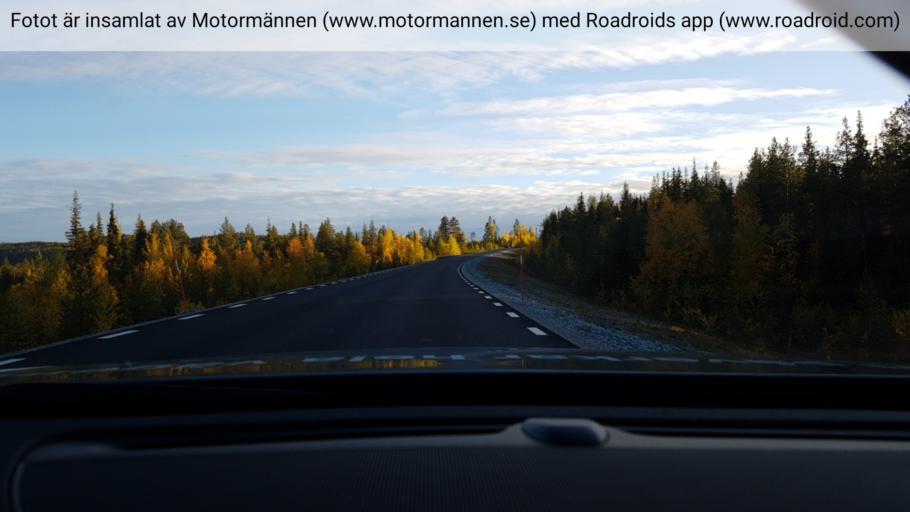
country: SE
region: Norrbotten
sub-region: Jokkmokks Kommun
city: Jokkmokk
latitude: 66.5751
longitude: 19.8052
